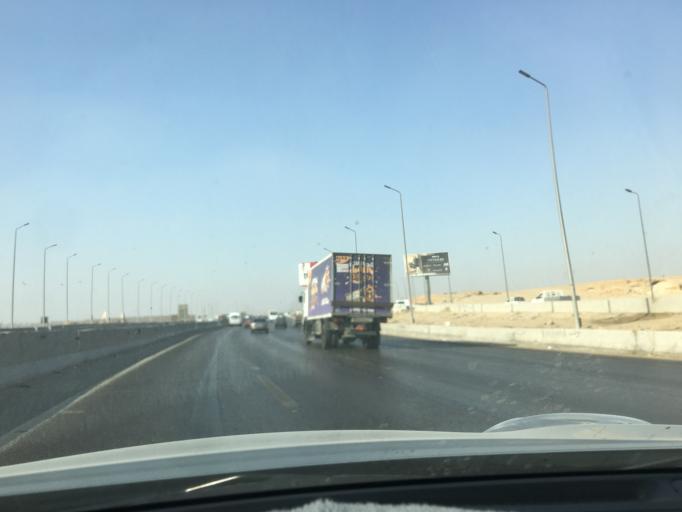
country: EG
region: Muhafazat al Qalyubiyah
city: Al Khankah
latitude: 30.0872
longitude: 31.4379
